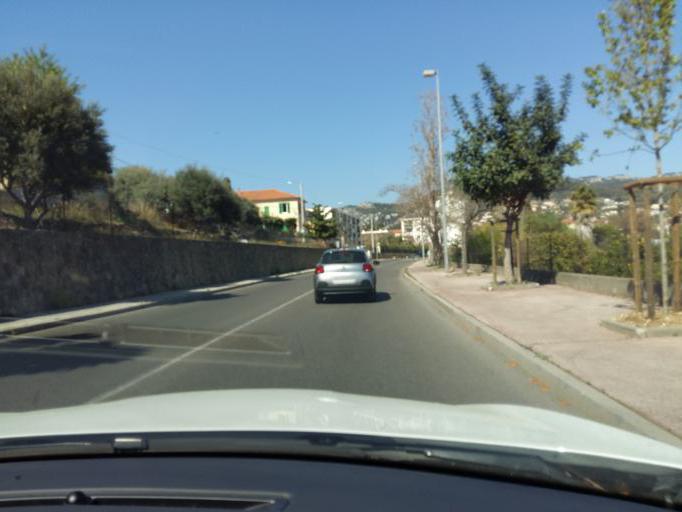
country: FR
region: Provence-Alpes-Cote d'Azur
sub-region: Departement du Var
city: Ollioules
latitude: 43.1307
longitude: 5.8442
